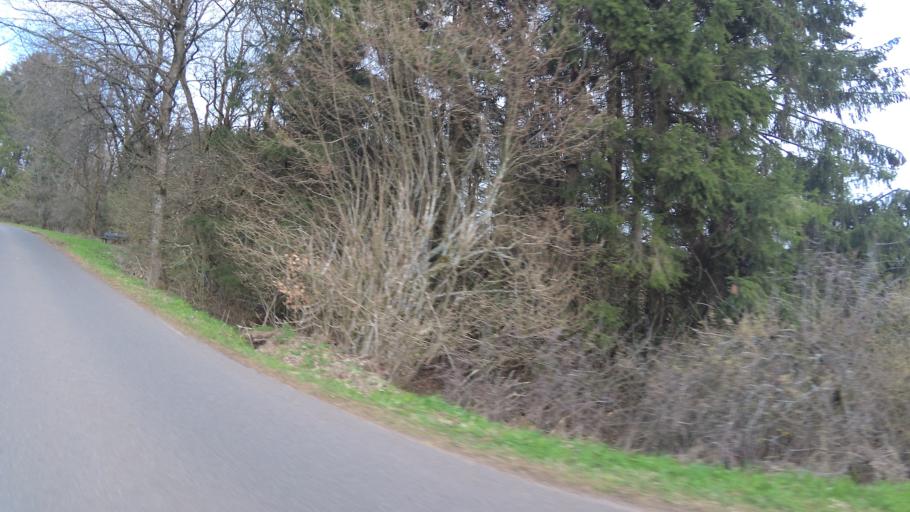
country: DE
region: Rheinland-Pfalz
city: Hahnweiler
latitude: 49.5689
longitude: 7.2191
